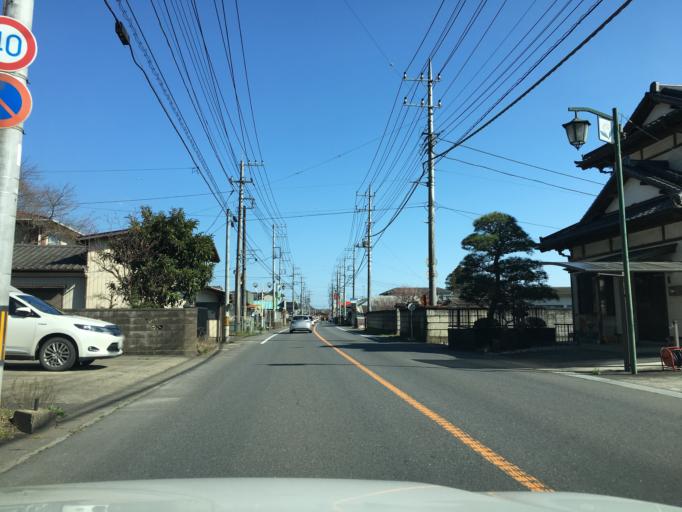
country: JP
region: Ibaraki
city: Omiya
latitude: 36.5515
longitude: 140.3255
